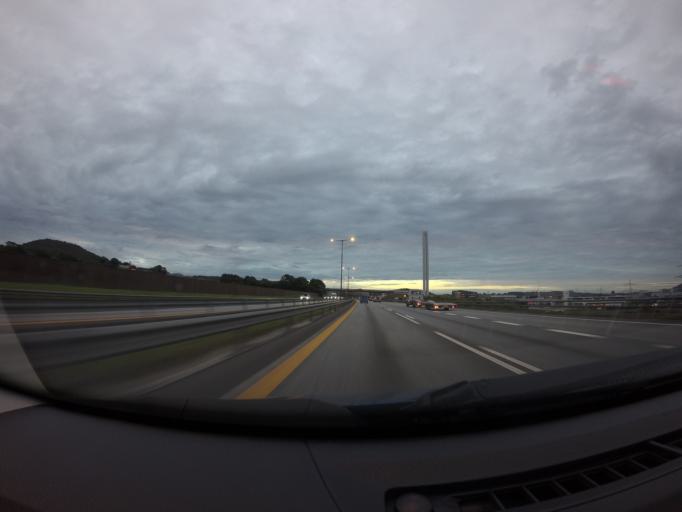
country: NO
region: Rogaland
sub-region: Sola
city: Sola
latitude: 58.9074
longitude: 5.6990
